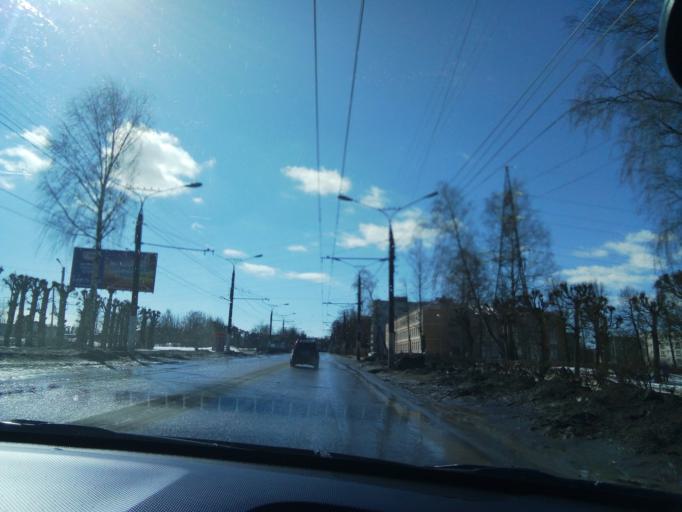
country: RU
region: Chuvashia
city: Novyye Lapsary
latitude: 56.1114
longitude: 47.1828
